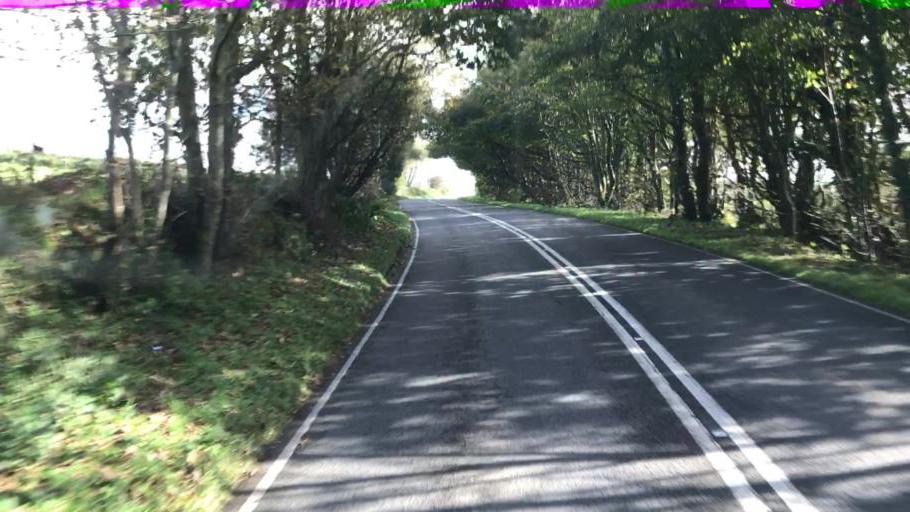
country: GB
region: England
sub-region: Cornwall
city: Callington
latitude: 50.5129
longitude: -4.2841
